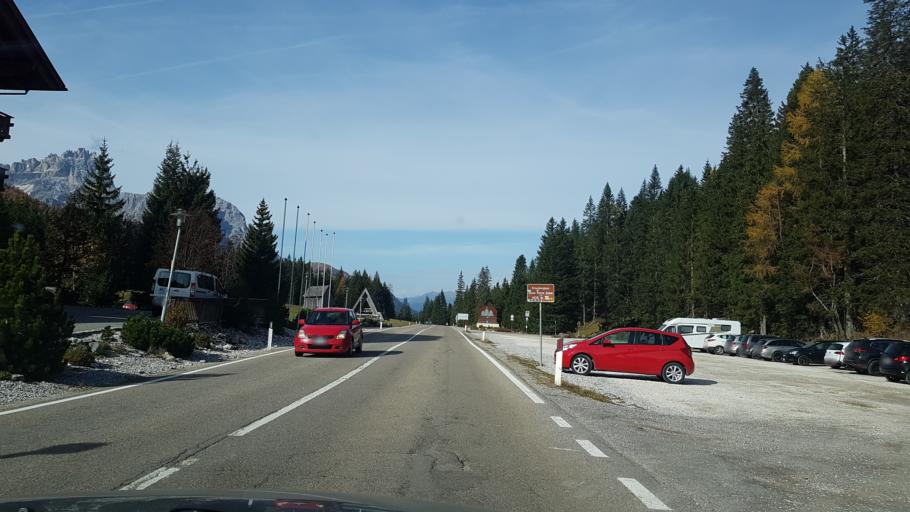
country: IT
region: Trentino-Alto Adige
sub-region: Bolzano
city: Sesto
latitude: 46.6557
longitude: 12.4204
